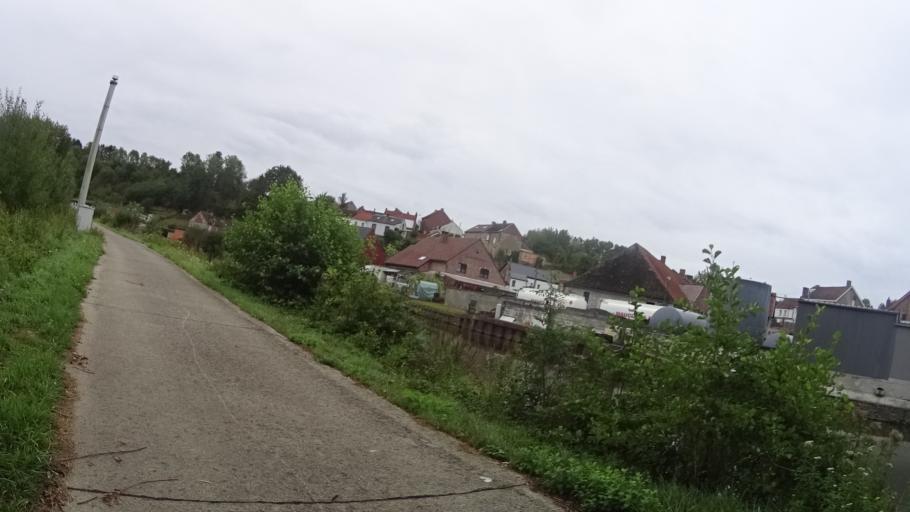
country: BE
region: Wallonia
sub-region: Province du Hainaut
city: Merbes-le-Chateau
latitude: 50.3211
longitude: 4.2162
